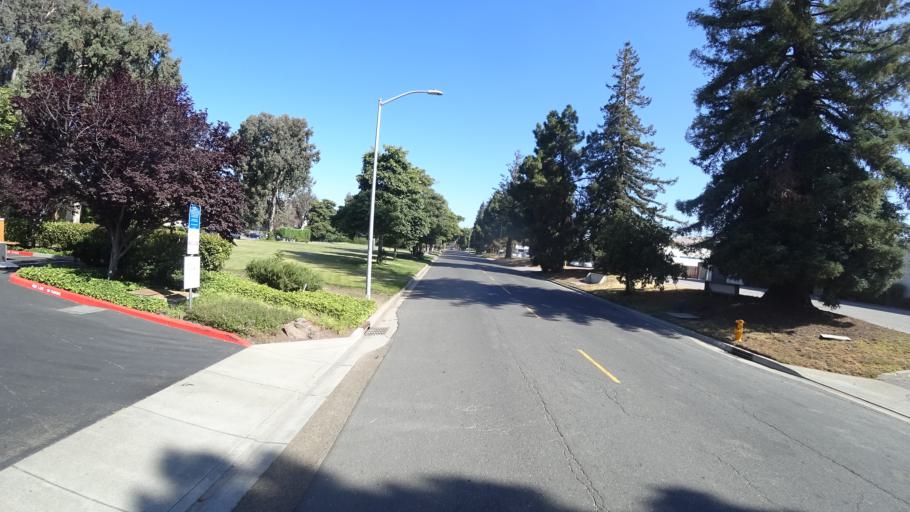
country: US
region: California
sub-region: Alameda County
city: Union City
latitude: 37.6163
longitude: -122.0486
